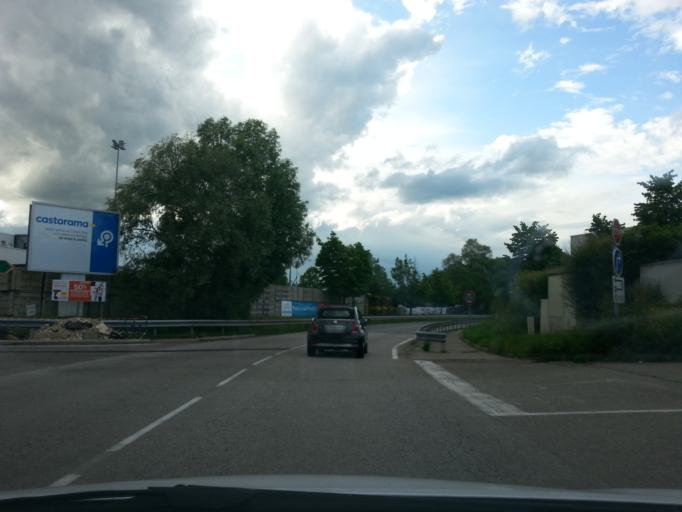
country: FR
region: Rhone-Alpes
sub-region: Departement du Rhone
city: Rillieux-la-Pape
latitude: 45.8274
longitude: 4.9113
